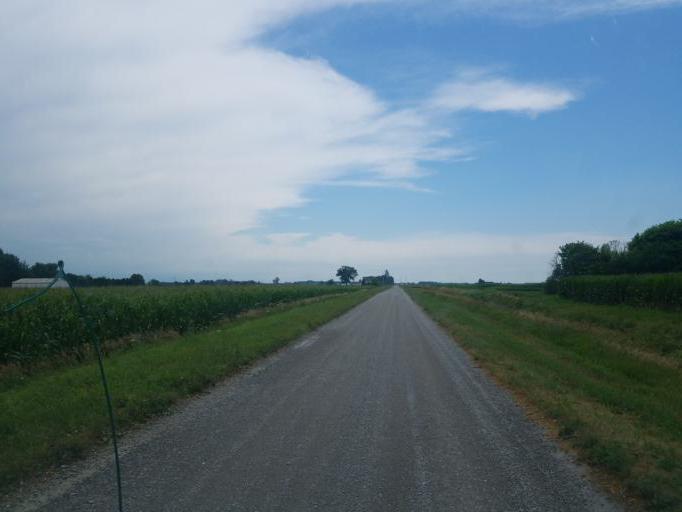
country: US
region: Ohio
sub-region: Defiance County
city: Hicksville
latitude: 41.2399
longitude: -84.8036
